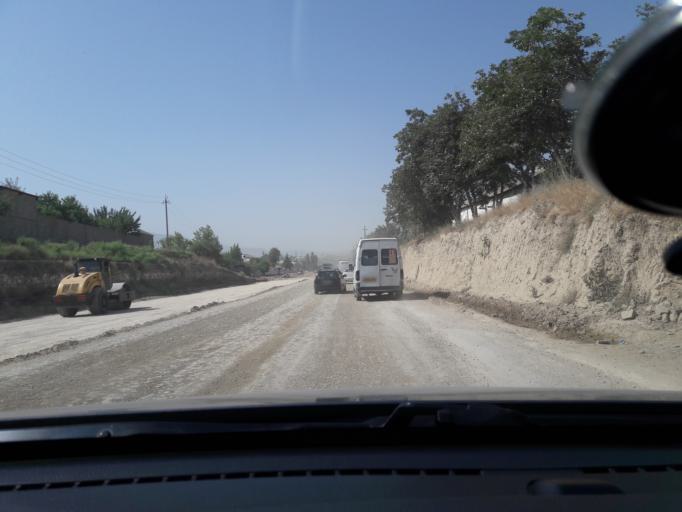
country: TJ
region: Dushanbe
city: Boshkengash
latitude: 38.4455
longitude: 68.7332
